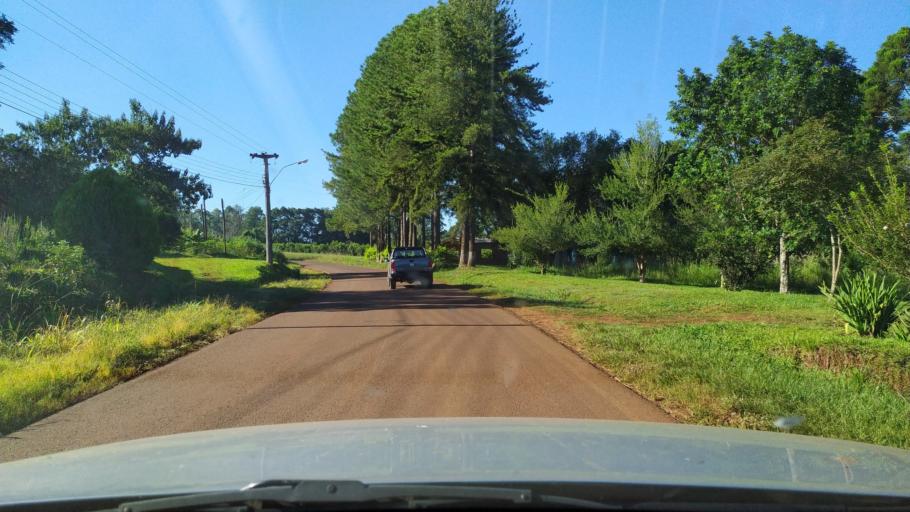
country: AR
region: Misiones
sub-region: Departamento de Montecarlo
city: Montecarlo
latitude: -26.6031
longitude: -54.7021
